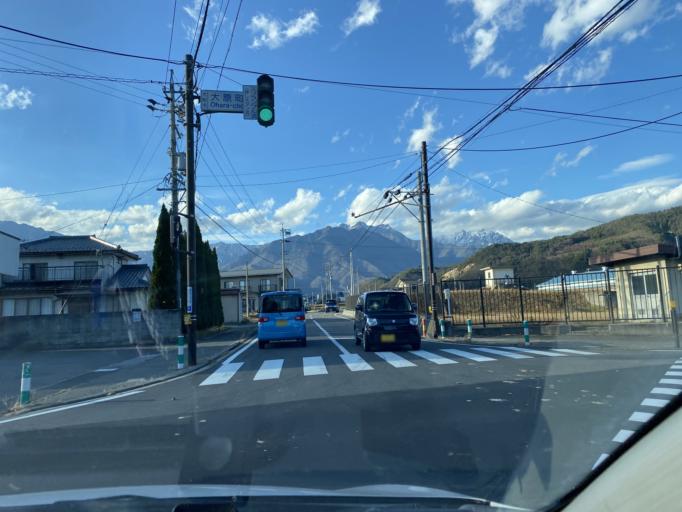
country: JP
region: Nagano
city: Omachi
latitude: 36.5225
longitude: 137.8336
